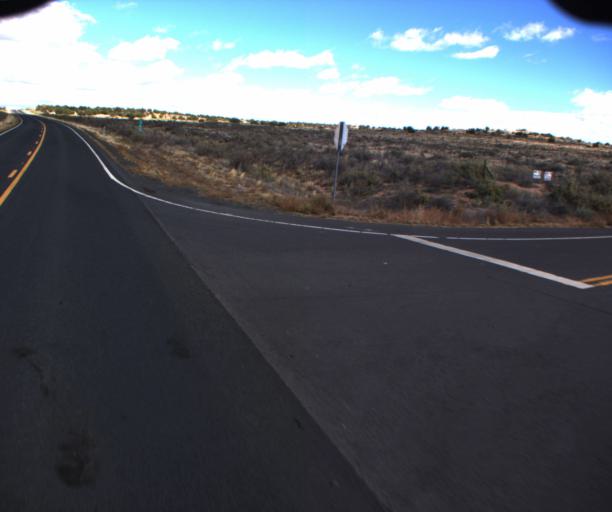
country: US
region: Arizona
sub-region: Apache County
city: Houck
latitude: 35.0972
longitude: -109.3126
